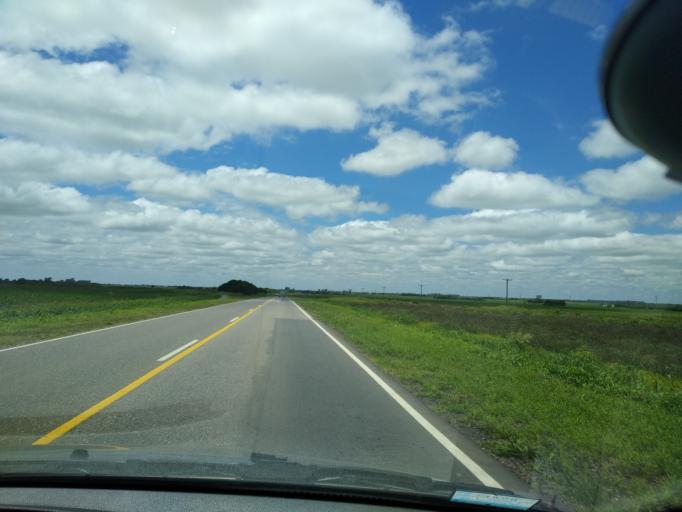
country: AR
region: Cordoba
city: Toledo
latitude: -31.6491
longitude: -64.1275
